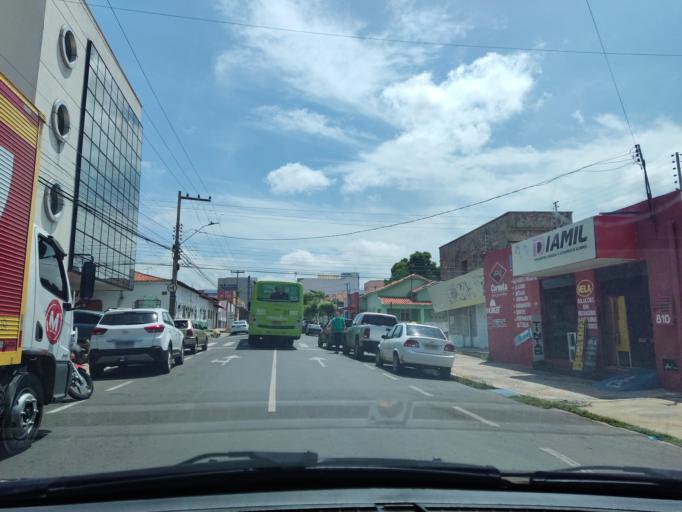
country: BR
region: Maranhao
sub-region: Timon
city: Timon
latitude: -5.0867
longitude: -42.8205
